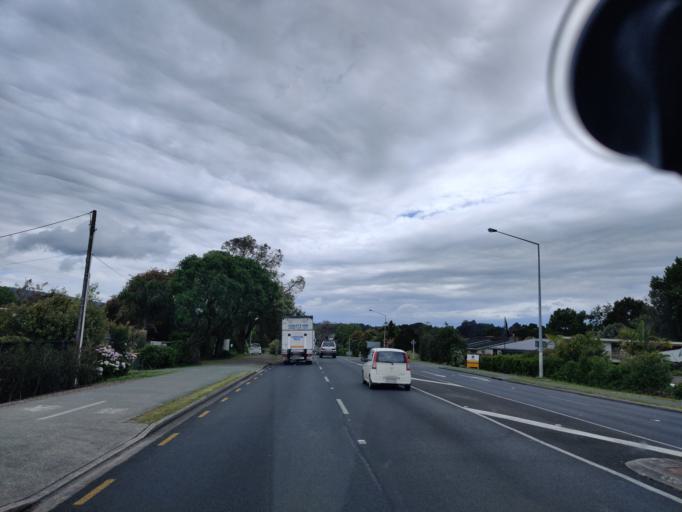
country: NZ
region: Auckland
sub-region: Auckland
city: Warkworth
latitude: -36.4022
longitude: 174.6589
